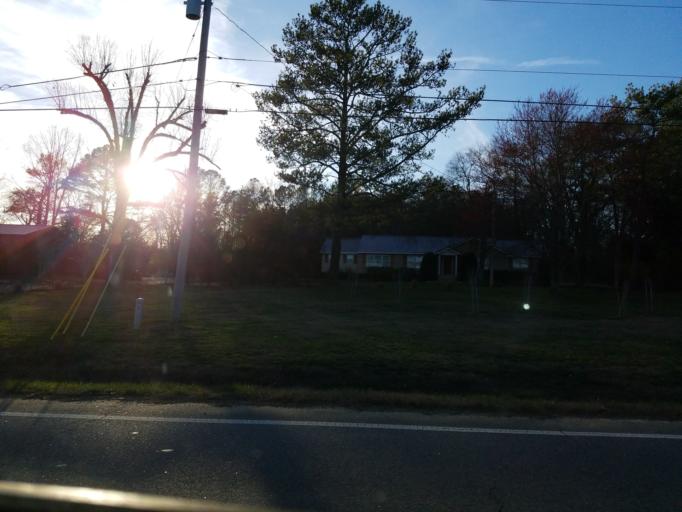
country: US
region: Georgia
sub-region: Gordon County
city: Calhoun
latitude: 34.5916
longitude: -84.9457
